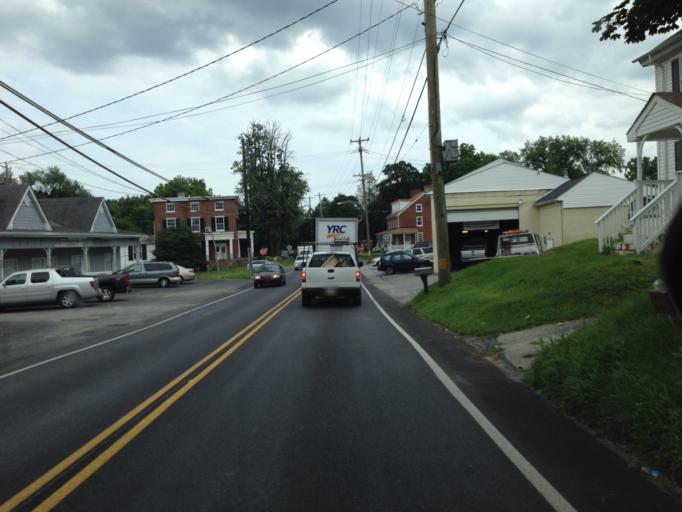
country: US
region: Pennsylvania
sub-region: Chester County
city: West Grove
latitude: 39.7829
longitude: -75.8764
